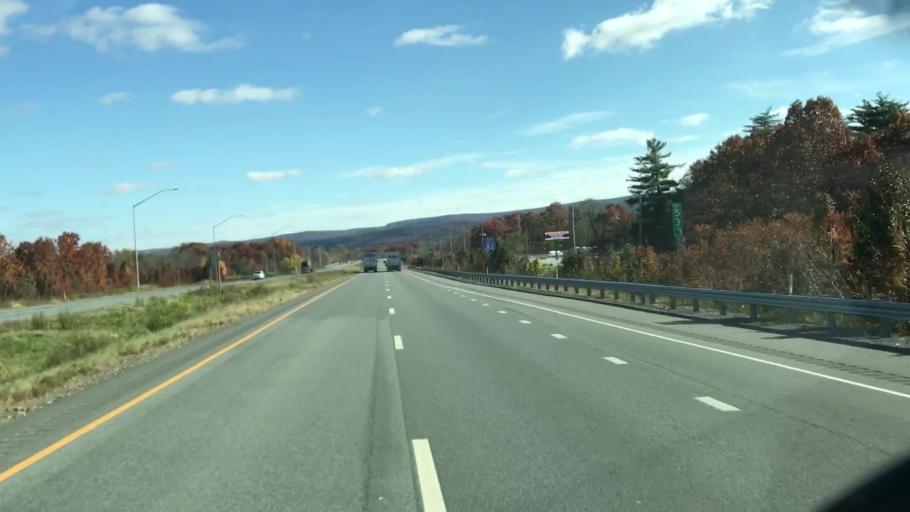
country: US
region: Pennsylvania
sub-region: Pike County
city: Matamoras
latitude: 41.3576
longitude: -74.7120
